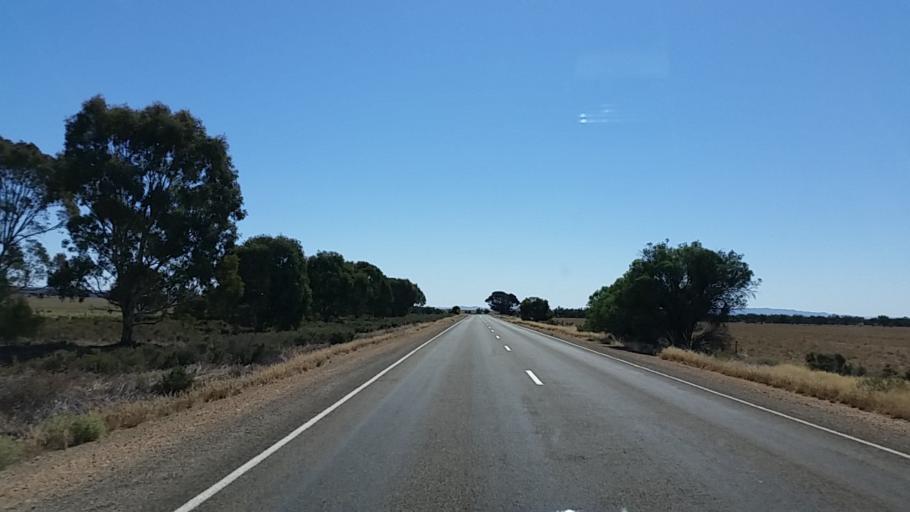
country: AU
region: South Australia
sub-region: Peterborough
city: Peterborough
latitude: -32.7666
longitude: 138.6575
